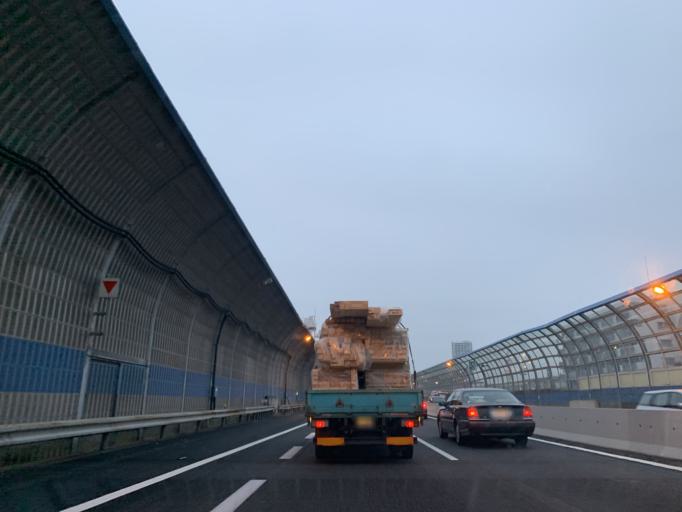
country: JP
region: Chiba
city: Funabashi
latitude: 35.6904
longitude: 139.9914
